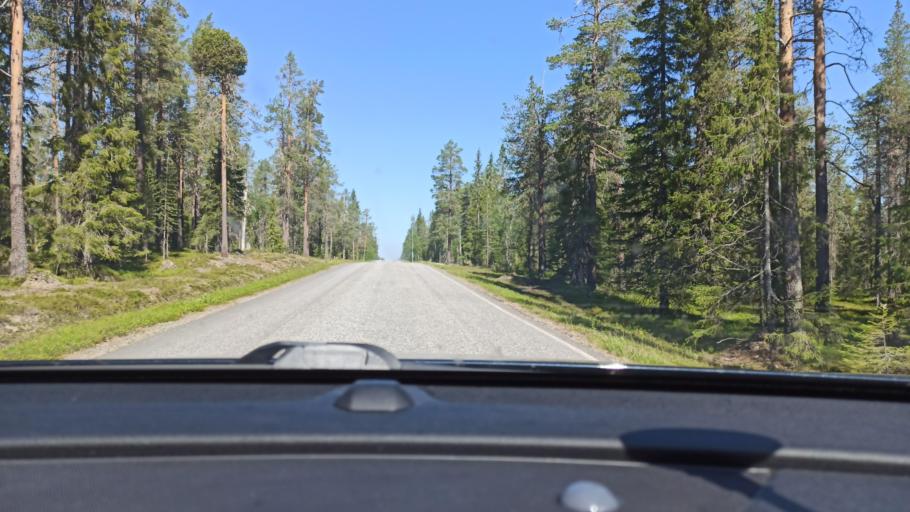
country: FI
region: Lapland
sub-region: Tunturi-Lappi
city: Kolari
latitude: 67.6724
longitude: 24.1480
